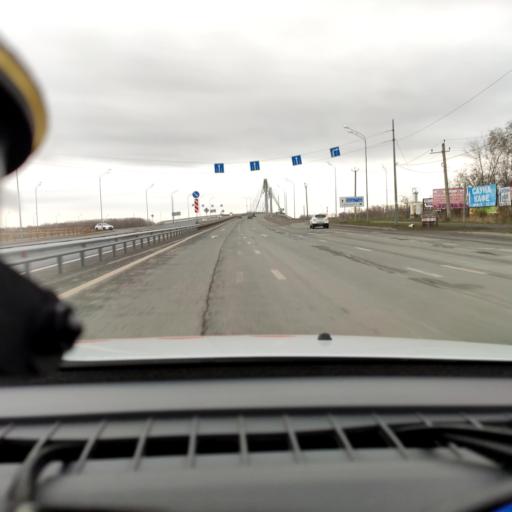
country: RU
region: Samara
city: Smyshlyayevka
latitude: 53.1855
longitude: 50.3019
